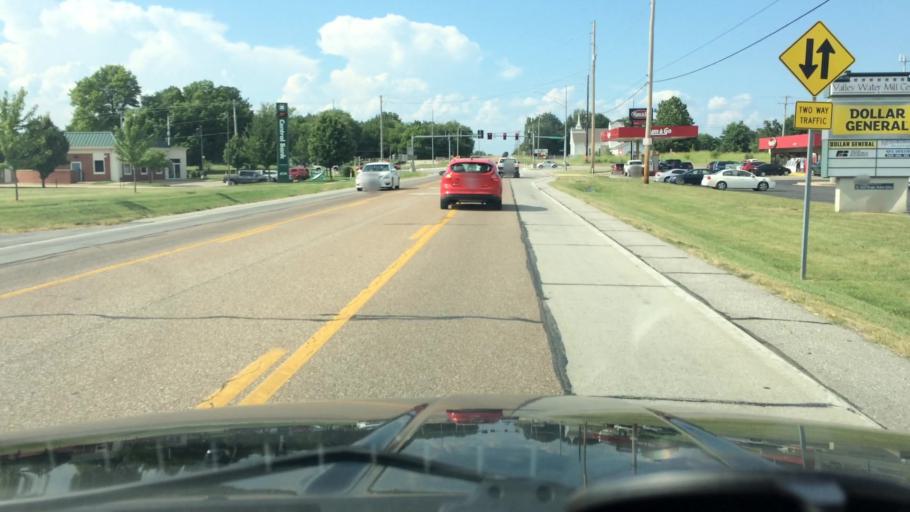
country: US
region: Missouri
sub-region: Greene County
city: Springfield
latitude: 37.2607
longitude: -93.2649
